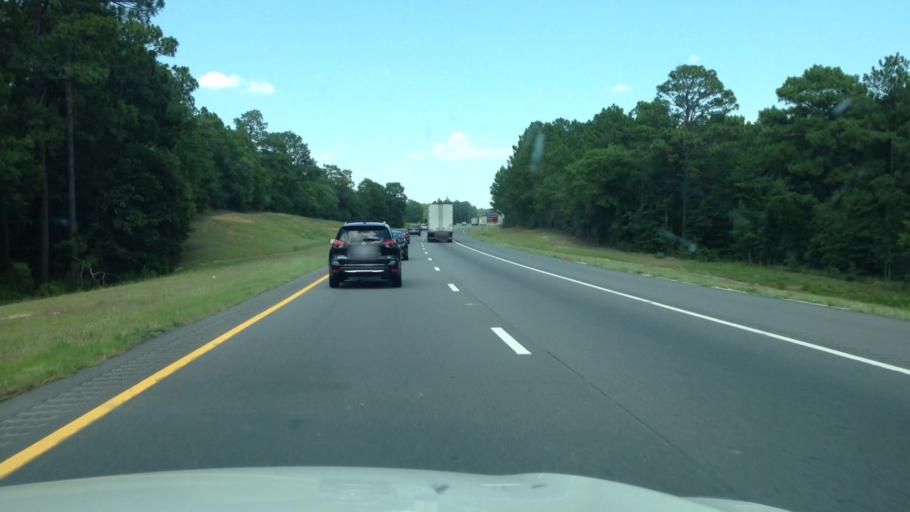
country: US
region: North Carolina
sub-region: Cumberland County
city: Hope Mills
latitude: 34.9676
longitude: -78.8805
